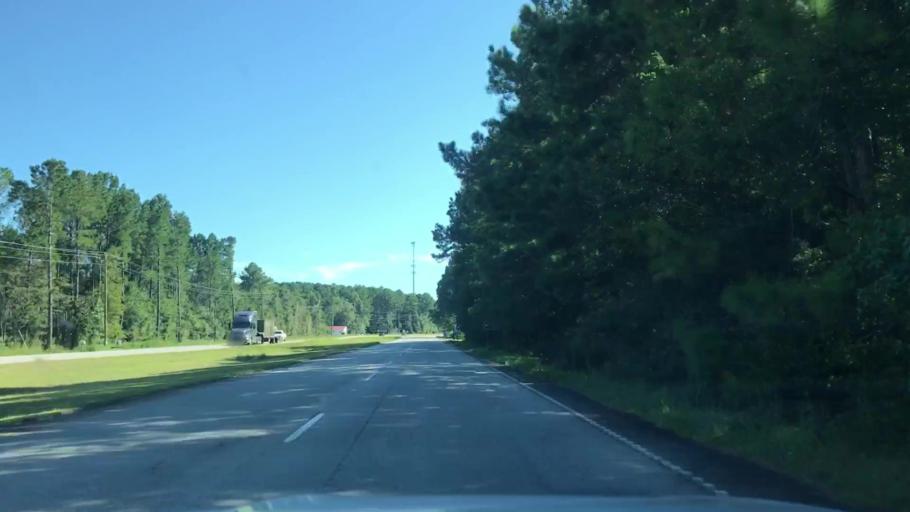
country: US
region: South Carolina
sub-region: Charleston County
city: Awendaw
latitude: 32.9938
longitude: -79.6454
